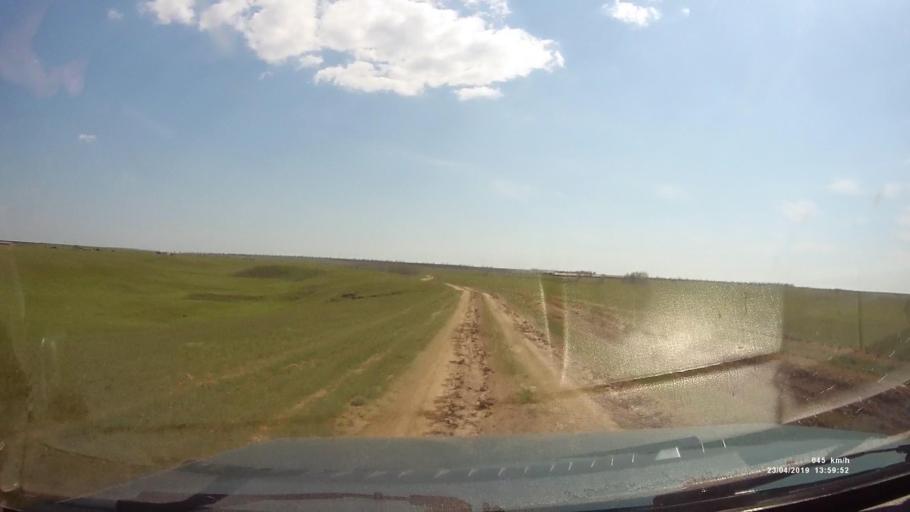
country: RU
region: Rostov
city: Remontnoye
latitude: 46.5635
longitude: 42.9469
